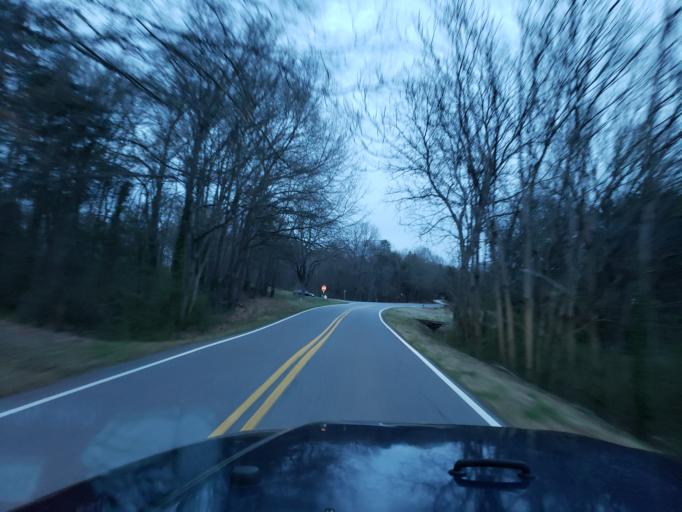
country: US
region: North Carolina
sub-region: Cleveland County
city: White Plains
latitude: 35.2398
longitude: -81.4587
